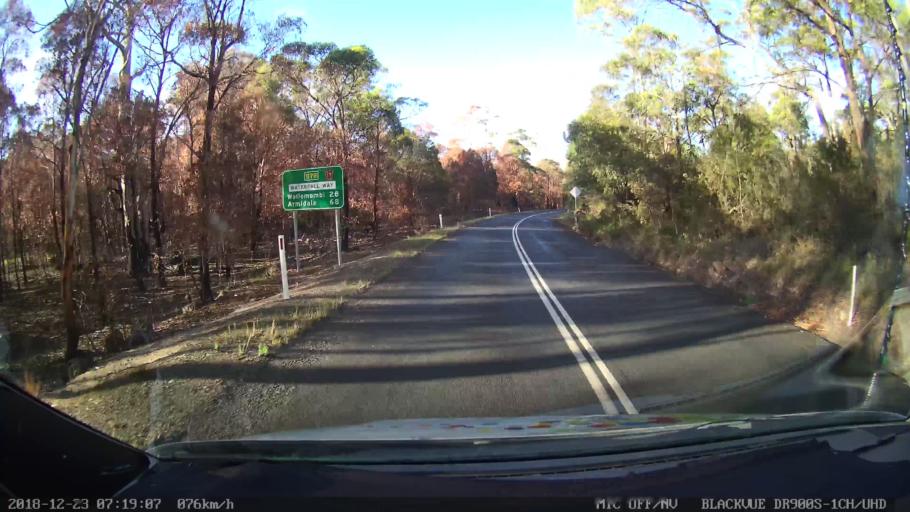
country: AU
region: New South Wales
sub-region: Bellingen
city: Dorrigo
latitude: -30.4828
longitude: 152.2908
